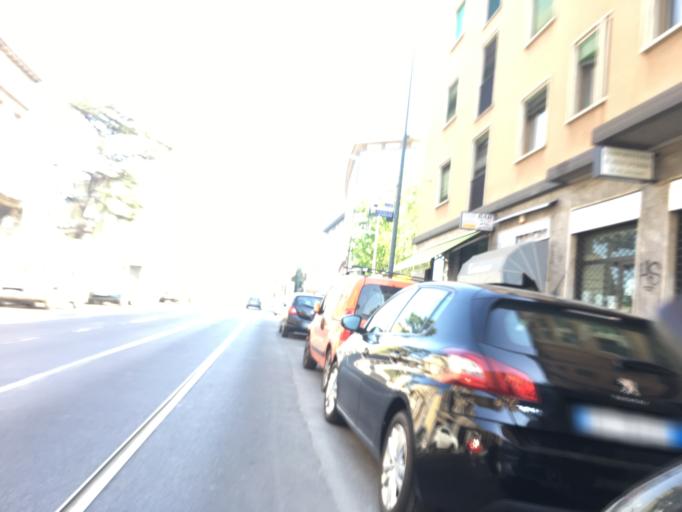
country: IT
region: Lombardy
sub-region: Citta metropolitana di Milano
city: Milano
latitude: 45.4401
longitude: 9.1999
